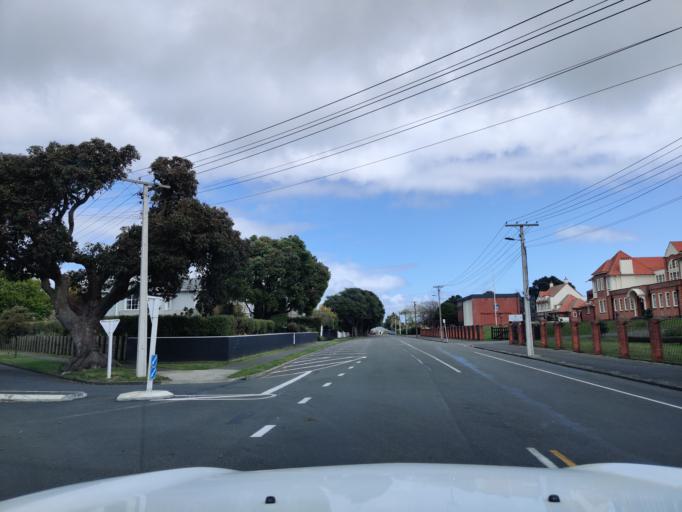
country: NZ
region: Manawatu-Wanganui
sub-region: Wanganui District
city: Wanganui
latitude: -39.9288
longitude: 175.0395
